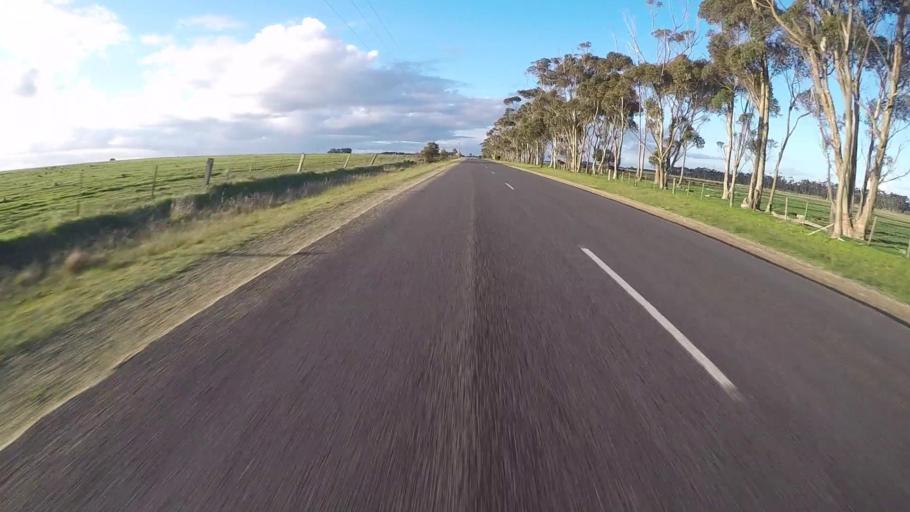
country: AU
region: Victoria
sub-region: Greater Geelong
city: Wandana Heights
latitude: -38.1274
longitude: 144.2038
